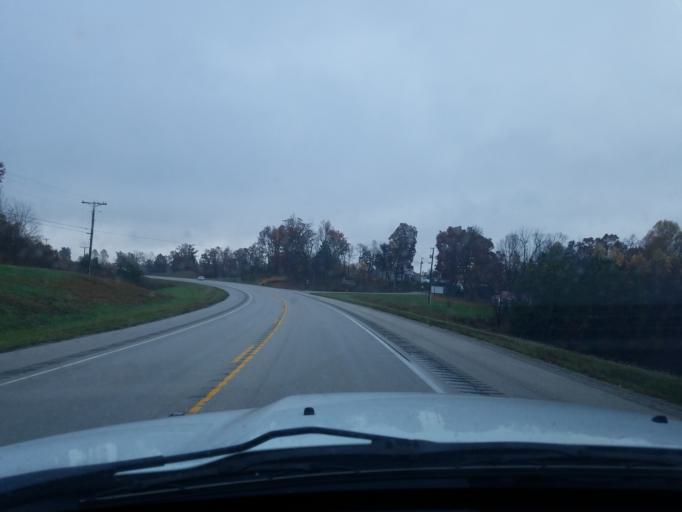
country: US
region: Kentucky
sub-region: Larue County
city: Hodgenville
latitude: 37.4665
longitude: -85.5807
